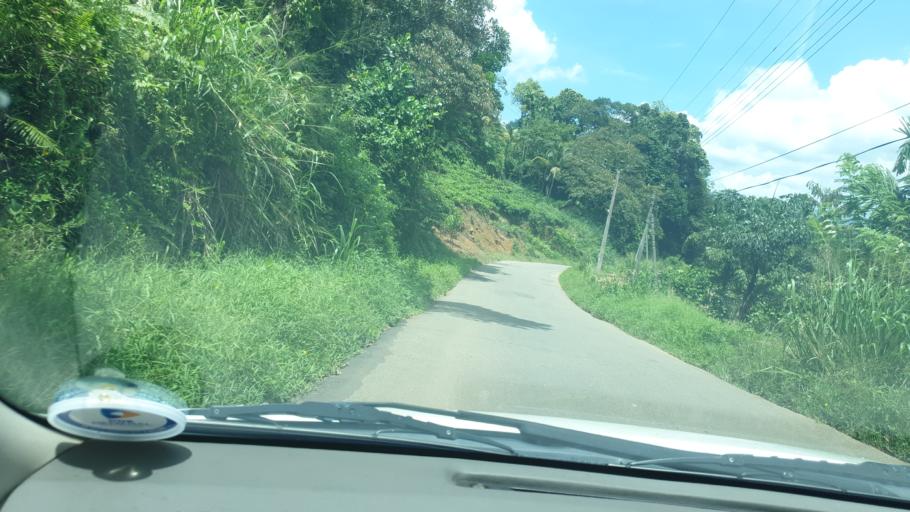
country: LK
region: Sabaragamuwa
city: Ratnapura
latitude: 6.4704
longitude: 80.4250
